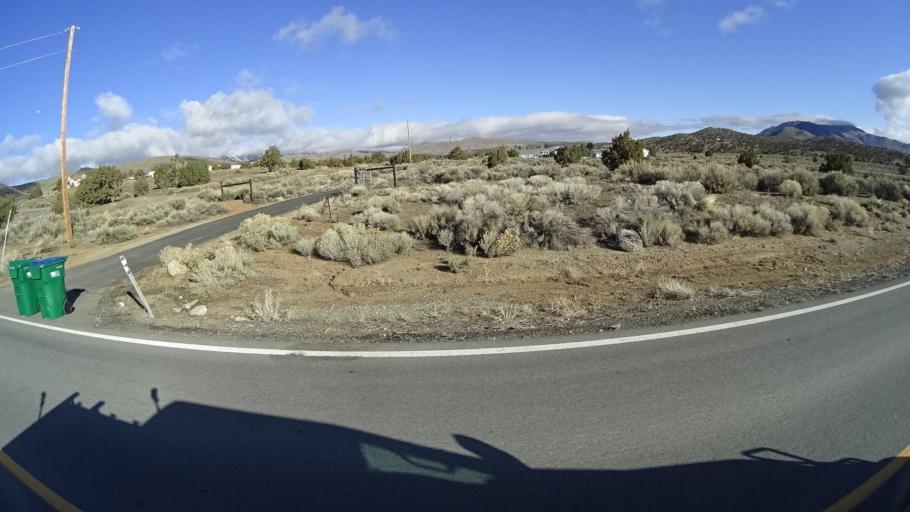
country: US
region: Nevada
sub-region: Washoe County
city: Cold Springs
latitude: 39.7154
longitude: -119.8963
